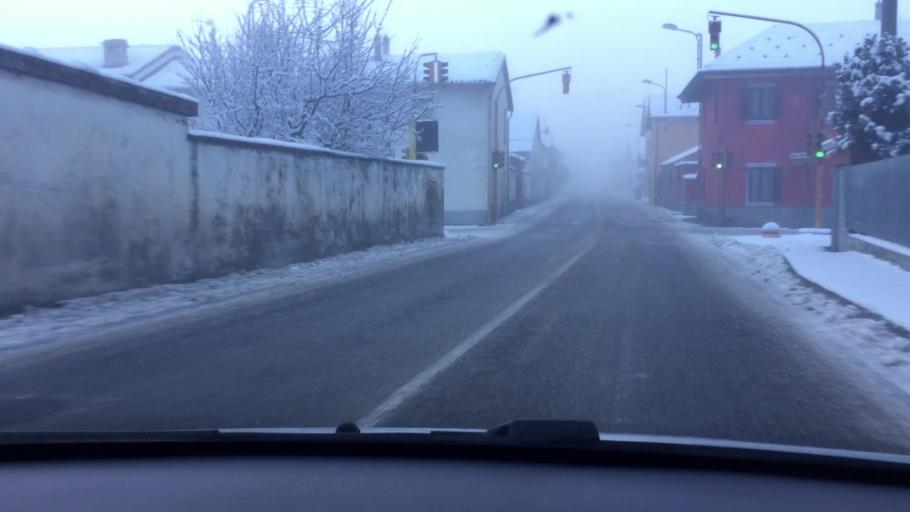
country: IT
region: Piedmont
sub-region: Provincia di Torino
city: Scalenghe
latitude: 44.8961
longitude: 7.4904
